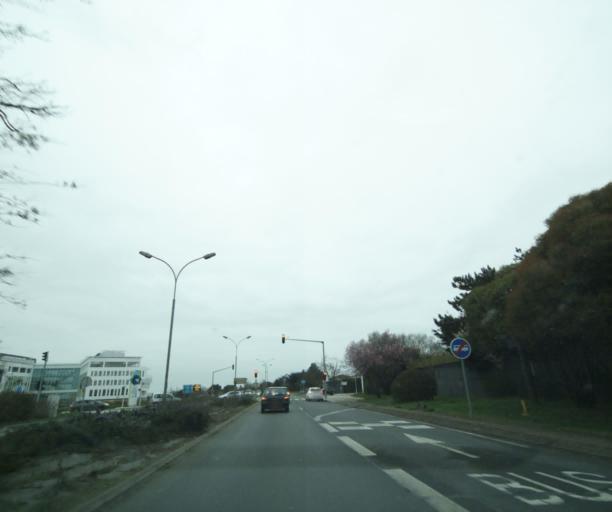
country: FR
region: Poitou-Charentes
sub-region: Departement de la Charente-Maritime
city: Lagord
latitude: 46.1867
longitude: -1.1506
